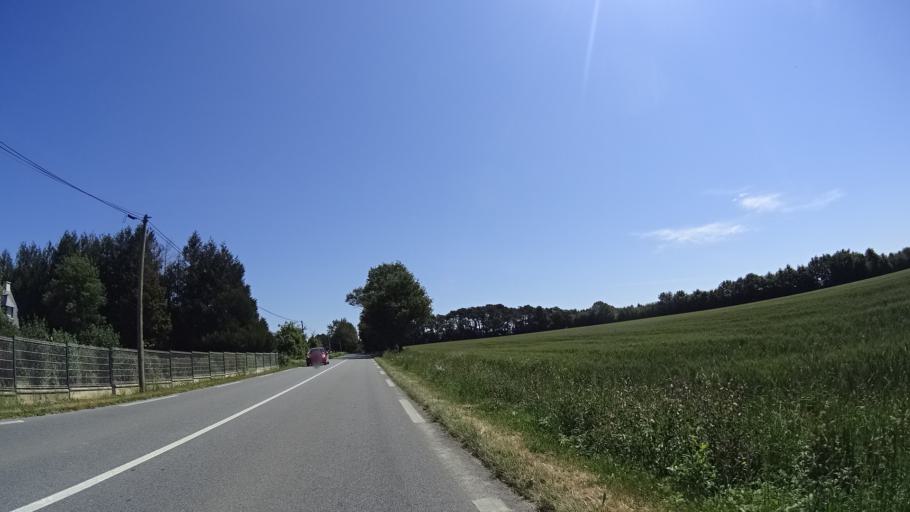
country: FR
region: Brittany
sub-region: Departement d'Ille-et-Vilaine
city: Messac
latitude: 47.8280
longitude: -1.7641
